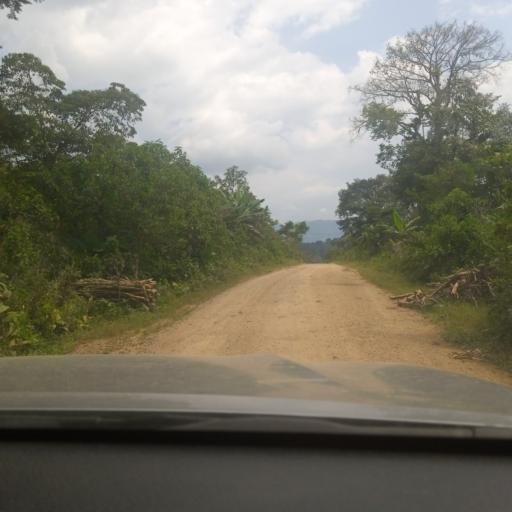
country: ET
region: Southern Nations, Nationalities, and People's Region
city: Tippi
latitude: 7.1334
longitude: 35.4256
